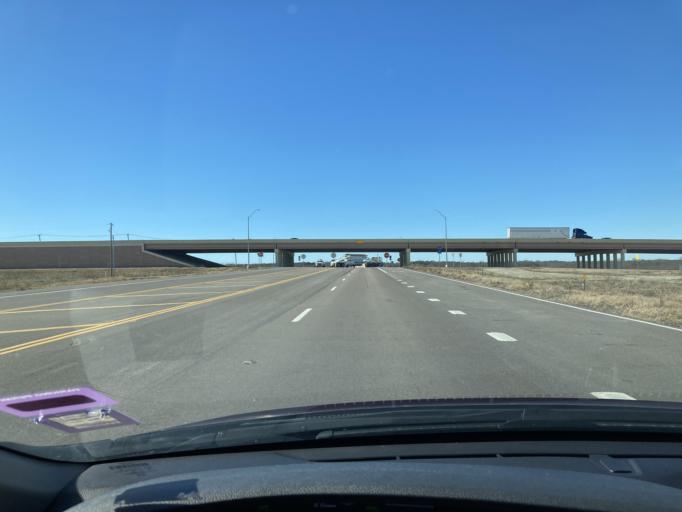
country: US
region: Texas
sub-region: Navarro County
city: Corsicana
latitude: 32.0425
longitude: -96.4452
